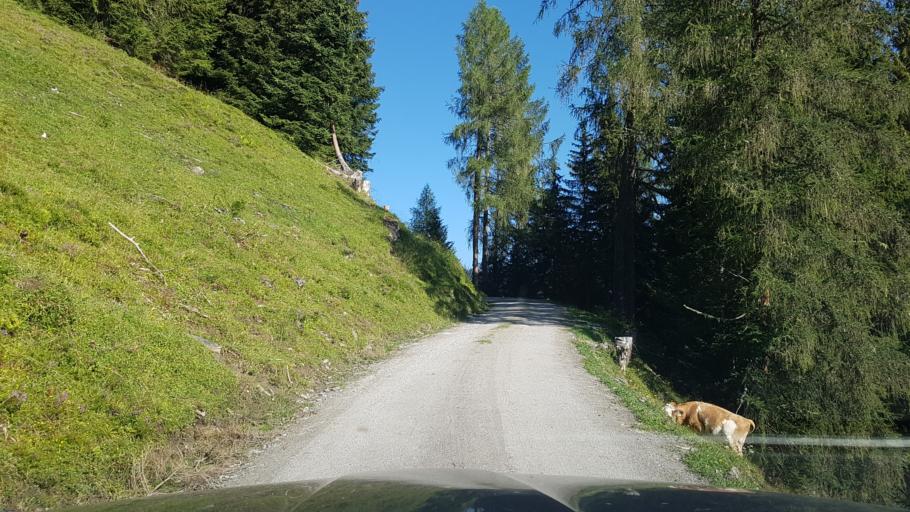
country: AT
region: Salzburg
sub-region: Politischer Bezirk Sankt Johann im Pongau
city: Dorfgastein
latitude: 47.2473
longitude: 13.0740
